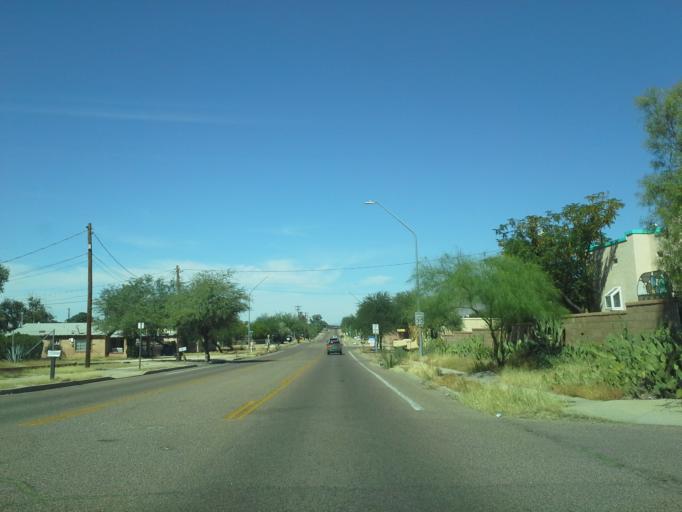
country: US
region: Arizona
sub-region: Pima County
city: South Tucson
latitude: 32.2404
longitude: -110.9688
